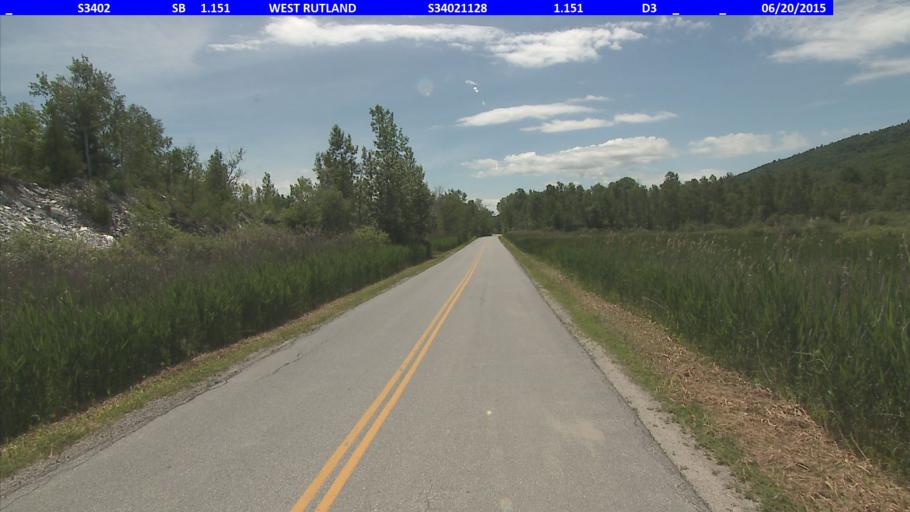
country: US
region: Vermont
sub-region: Rutland County
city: West Rutland
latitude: 43.6099
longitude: -73.0564
